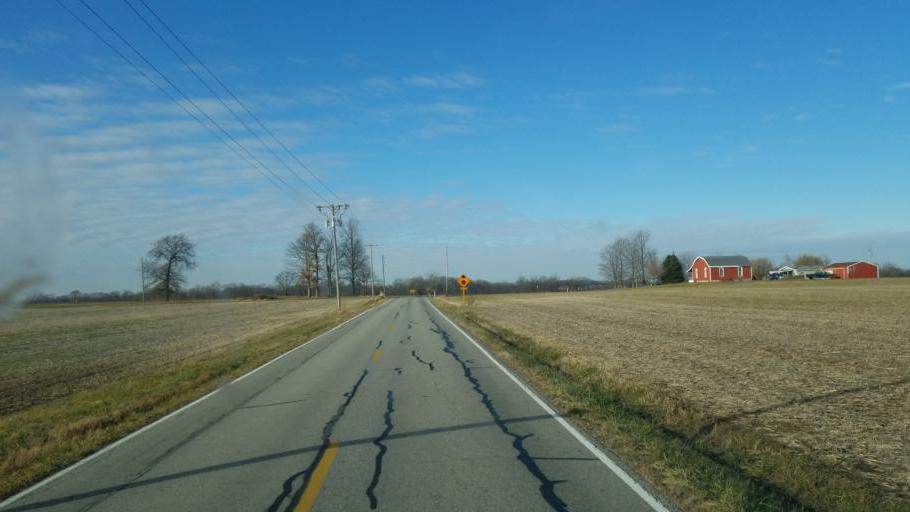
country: US
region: Ohio
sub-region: Marion County
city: Marion
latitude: 40.5351
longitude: -83.1871
